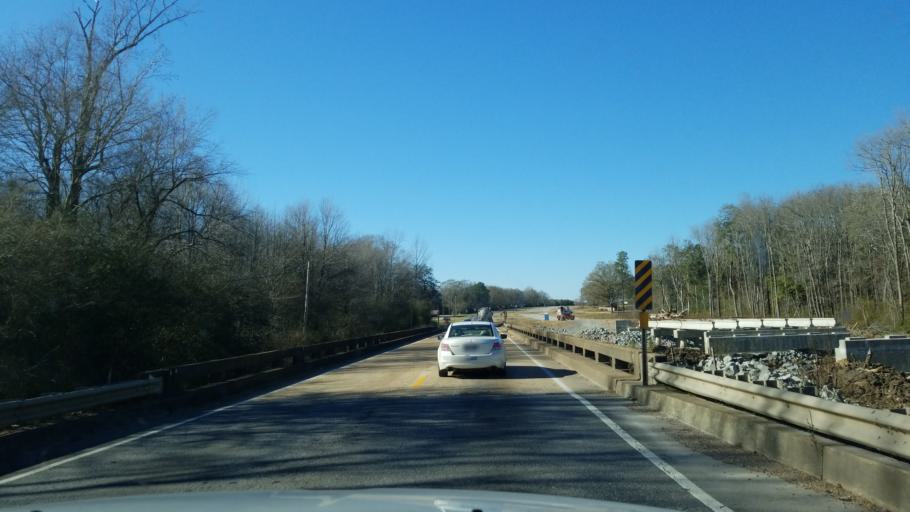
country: US
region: Alabama
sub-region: Pickens County
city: Gordo
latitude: 33.3346
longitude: -87.9258
